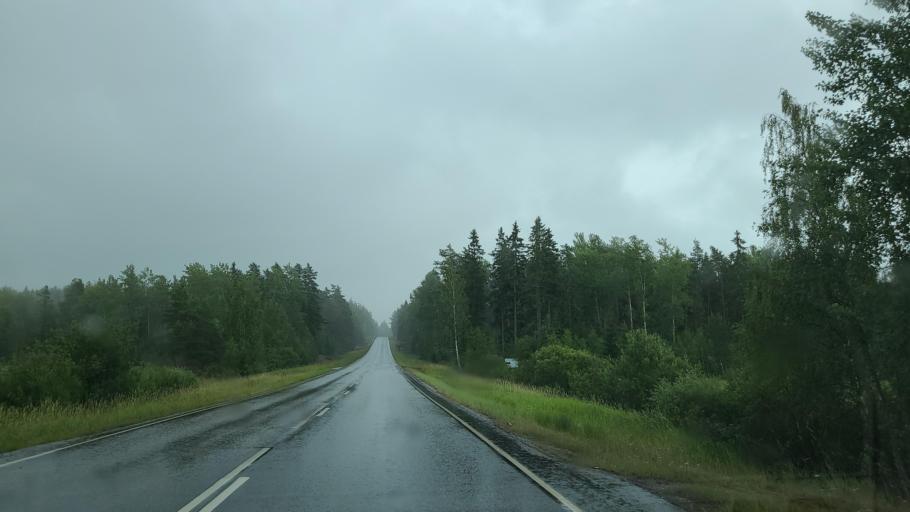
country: FI
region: Varsinais-Suomi
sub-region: Aboland-Turunmaa
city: Kimito
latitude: 60.2033
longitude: 22.6522
